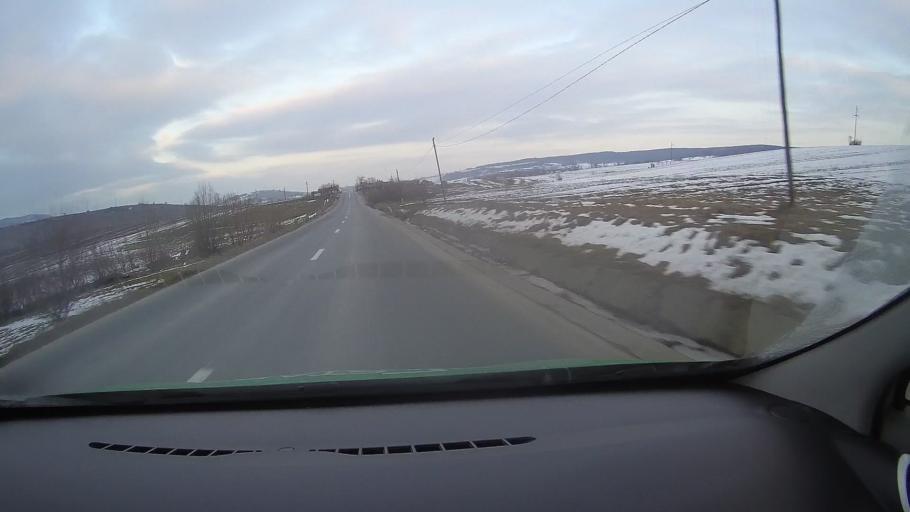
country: RO
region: Harghita
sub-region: Comuna Lupeni
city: Lupeni
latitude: 46.3566
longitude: 25.2088
